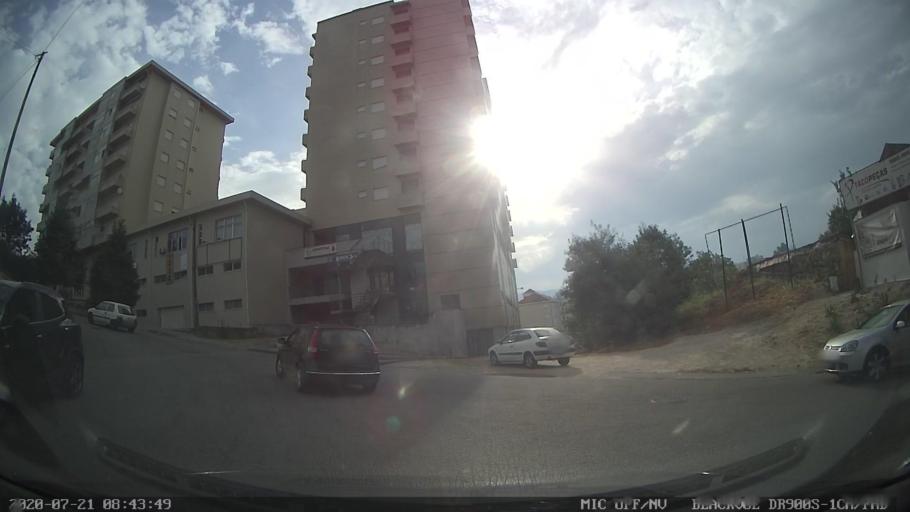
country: PT
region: Porto
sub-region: Amarante
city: Amarante
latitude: 41.2740
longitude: -8.0848
